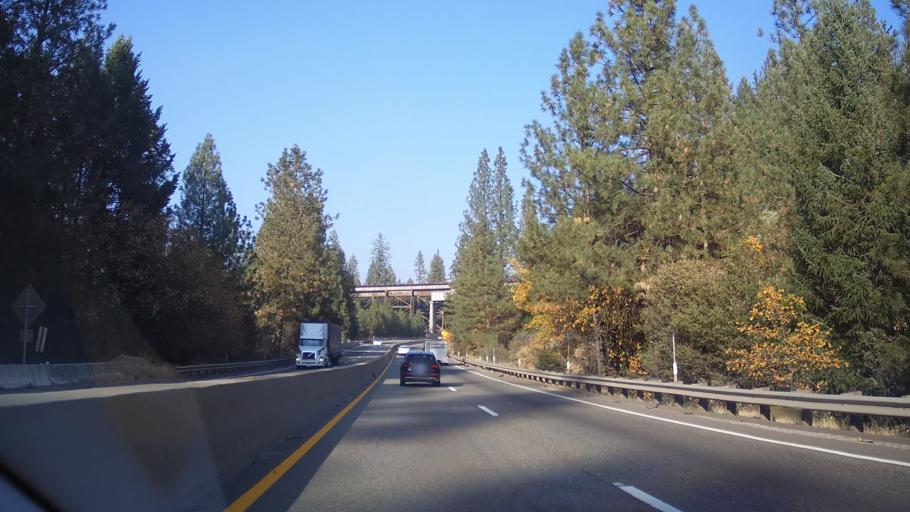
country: US
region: California
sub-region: Placer County
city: Colfax
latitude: 39.1203
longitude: -120.9412
